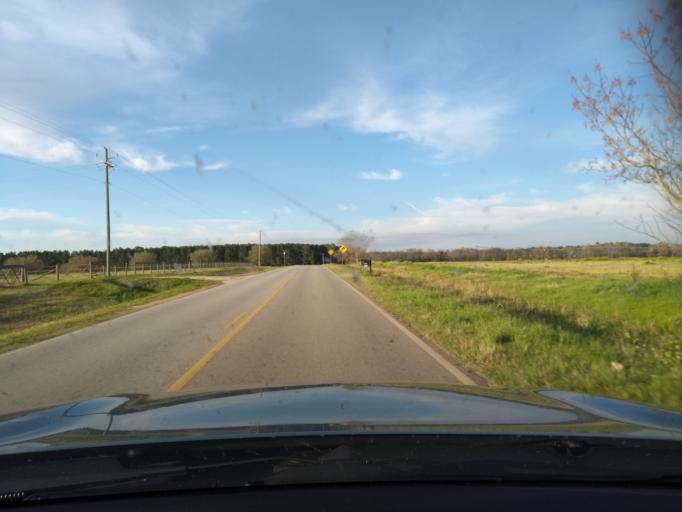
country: US
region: Georgia
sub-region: Bulloch County
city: Statesboro
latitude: 32.3293
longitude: -81.7749
